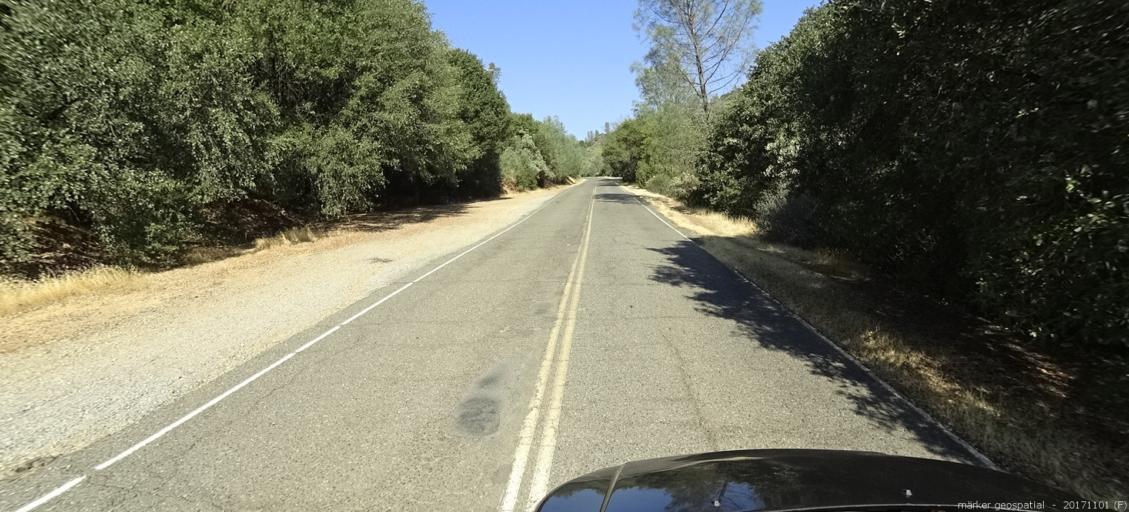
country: US
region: California
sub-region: Shasta County
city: Central Valley (historical)
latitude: 40.7061
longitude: -122.4050
